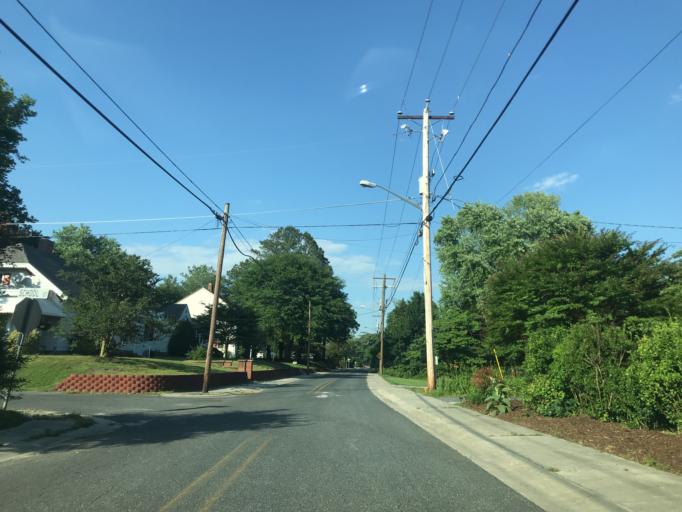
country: US
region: Maryland
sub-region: Wicomico County
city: Hebron
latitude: 38.5374
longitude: -75.7202
